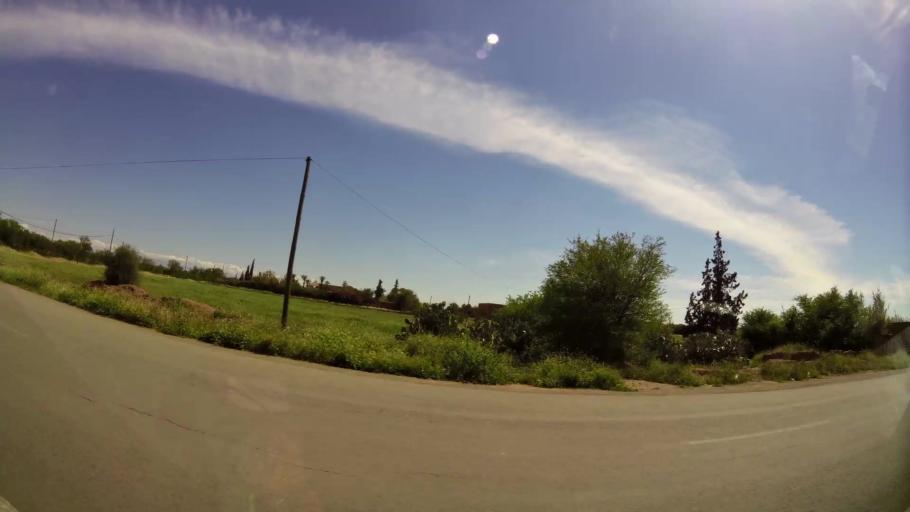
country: MA
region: Marrakech-Tensift-Al Haouz
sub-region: Marrakech
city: Marrakesh
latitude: 31.6400
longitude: -8.0926
